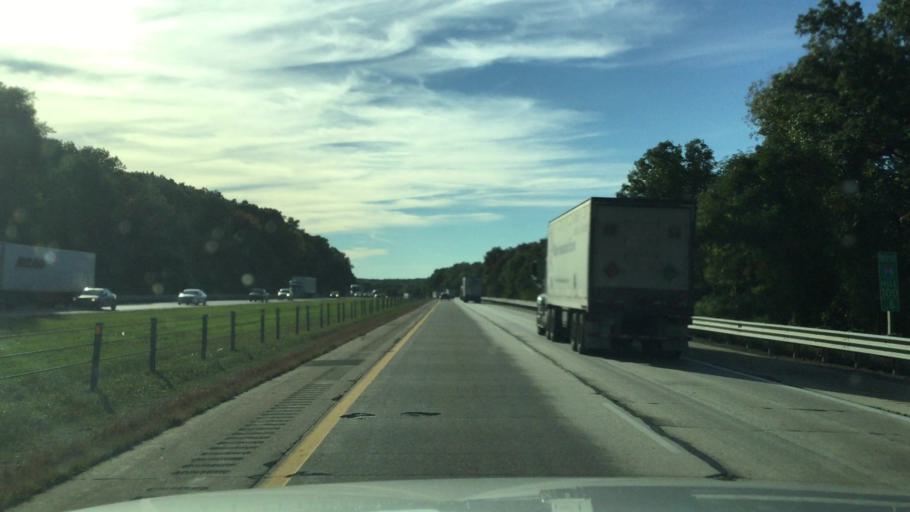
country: US
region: Michigan
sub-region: Calhoun County
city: Brownlee Park
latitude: 42.2856
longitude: -85.1409
